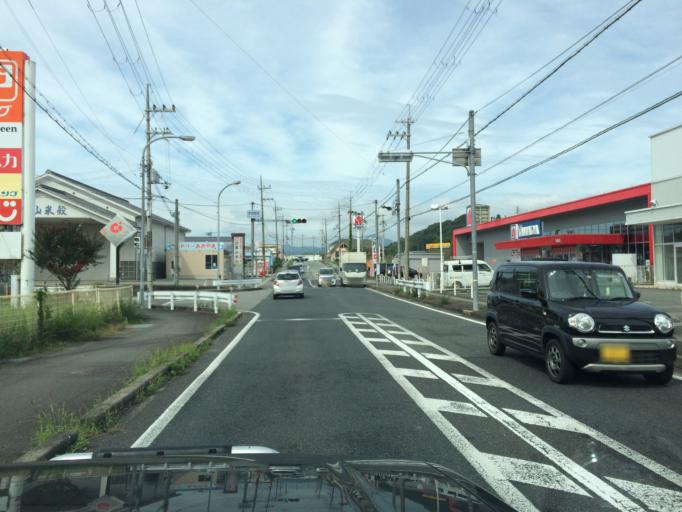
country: JP
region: Hyogo
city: Sasayama
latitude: 35.0713
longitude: 135.2103
